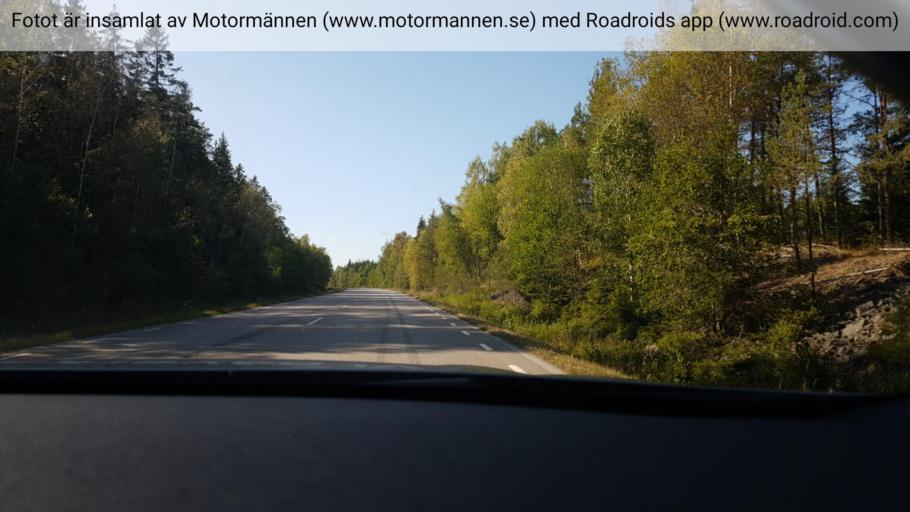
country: SE
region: Vaestra Goetaland
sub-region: Gotene Kommun
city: Goetene
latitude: 58.6206
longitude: 13.4809
